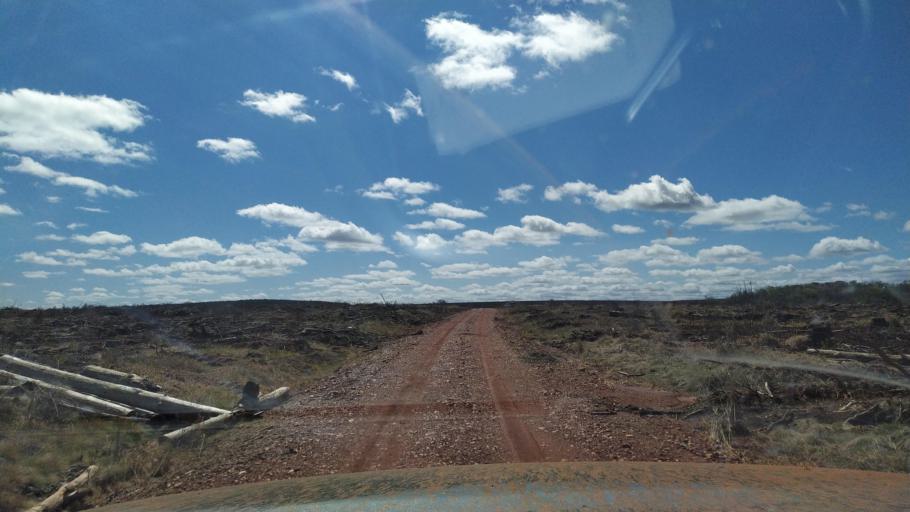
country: AR
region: Corrientes
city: Gobernador Ingeniero Valentin Virasoro
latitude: -28.2960
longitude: -56.0533
